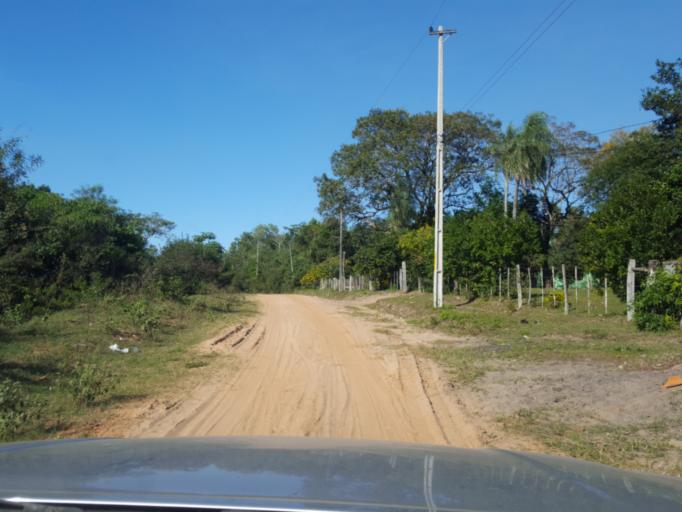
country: PY
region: Cordillera
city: Atyra
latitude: -25.2450
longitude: -57.1325
